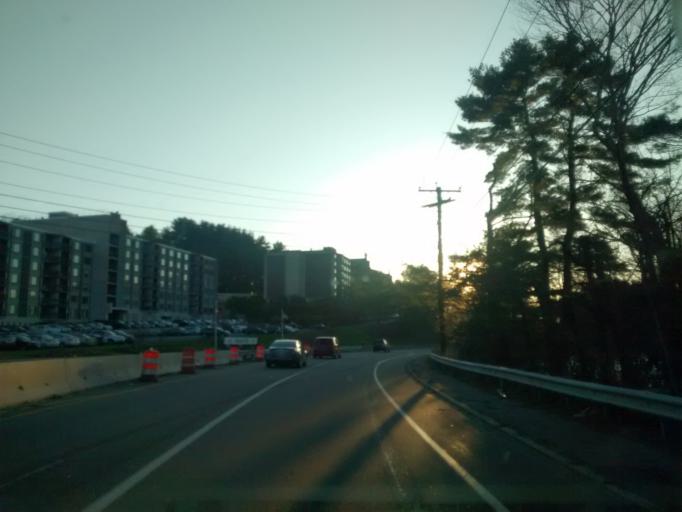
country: US
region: Massachusetts
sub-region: Middlesex County
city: Framingham Center
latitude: 42.2935
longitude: -71.4602
